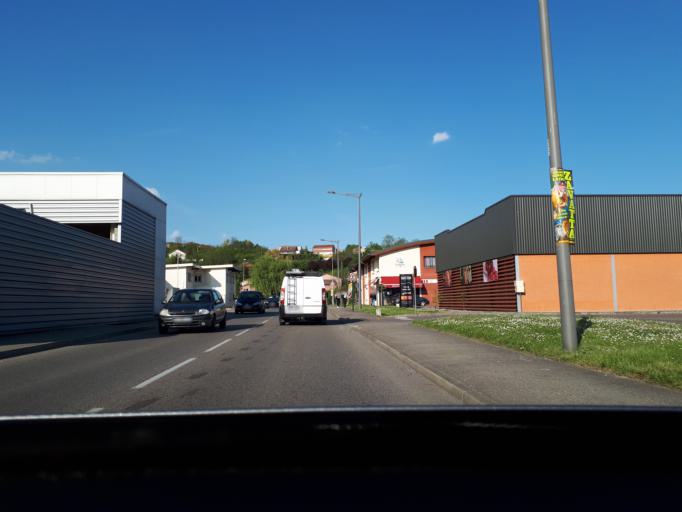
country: FR
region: Rhone-Alpes
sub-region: Departement de l'Isere
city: L'Isle-d'Abeau
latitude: 45.6155
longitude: 5.2343
